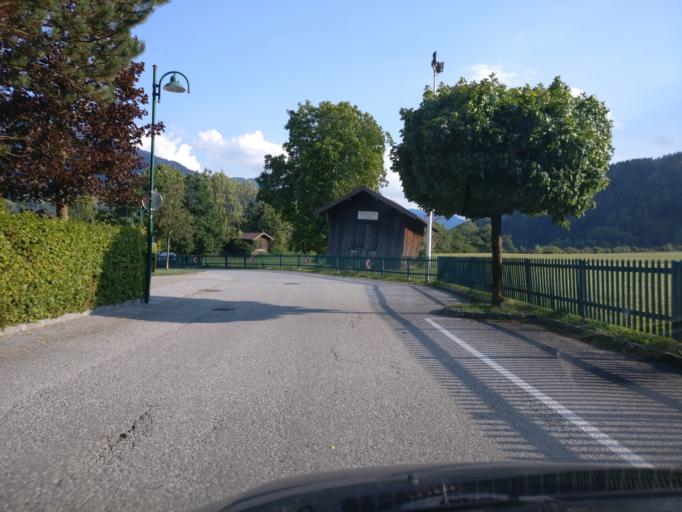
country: AT
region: Salzburg
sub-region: Politischer Bezirk Sankt Johann im Pongau
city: Bischofshofen
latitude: 47.4139
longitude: 13.2143
